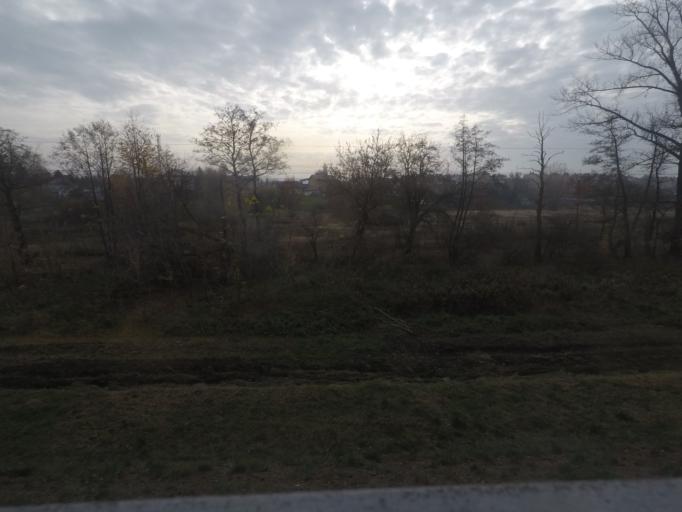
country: PL
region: Subcarpathian Voivodeship
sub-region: Powiat debicki
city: Debica
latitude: 50.0602
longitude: 21.4300
